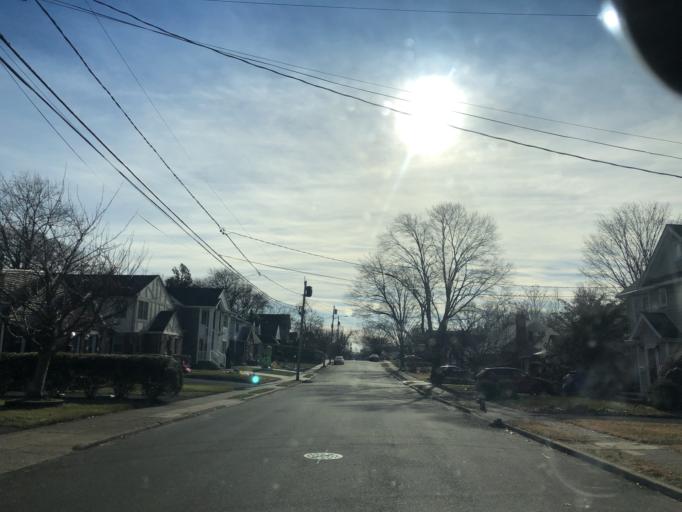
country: US
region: New Jersey
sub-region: Bergen County
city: Fair Lawn
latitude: 40.9297
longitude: -74.1342
